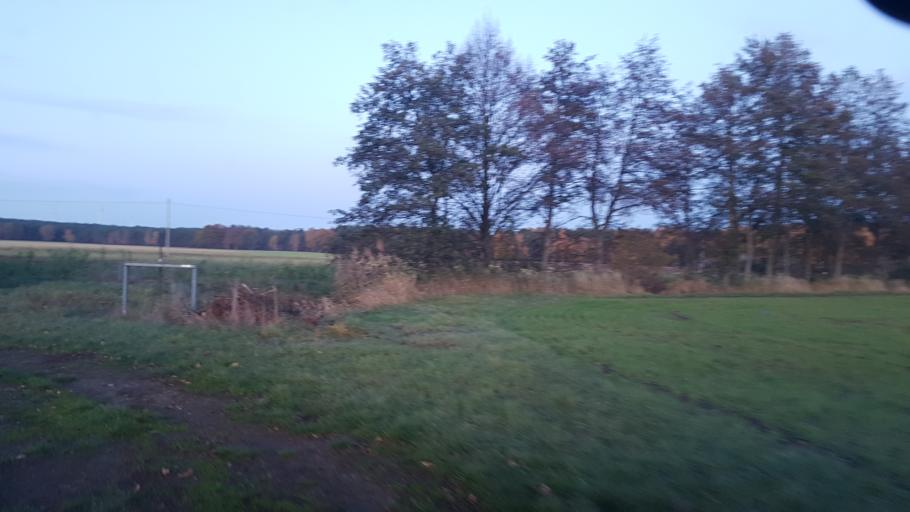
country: DE
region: Brandenburg
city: Schilda
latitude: 51.6342
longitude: 13.3408
